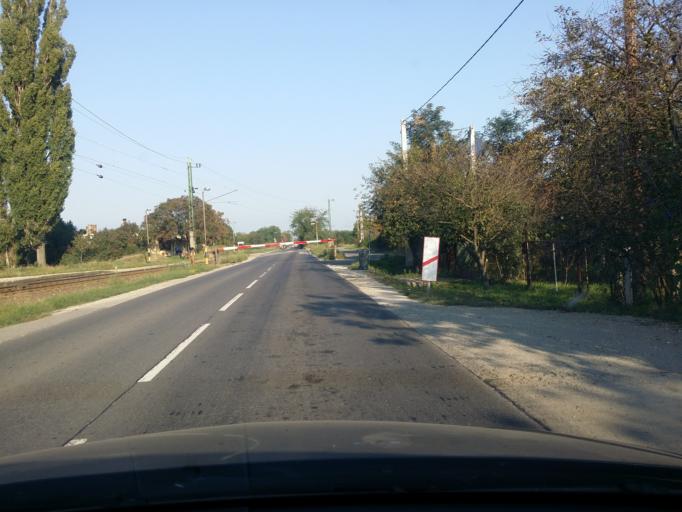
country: HU
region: Pest
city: Szodliget
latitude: 47.7524
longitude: 19.1647
